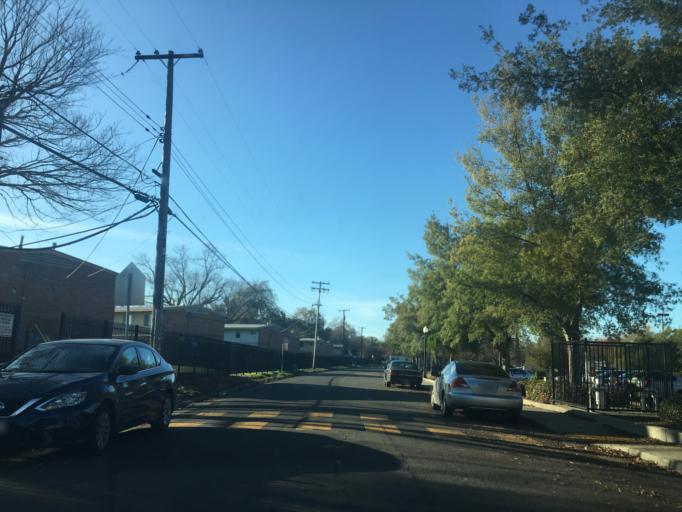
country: US
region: California
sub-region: Sacramento County
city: Sacramento
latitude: 38.5611
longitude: -121.5107
